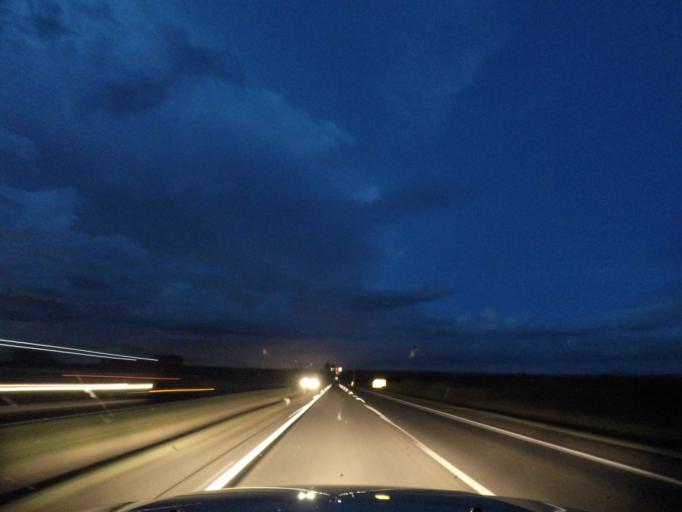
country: BR
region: Minas Gerais
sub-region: Uberlandia
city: Uberlandia
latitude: -19.2068
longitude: -48.1497
